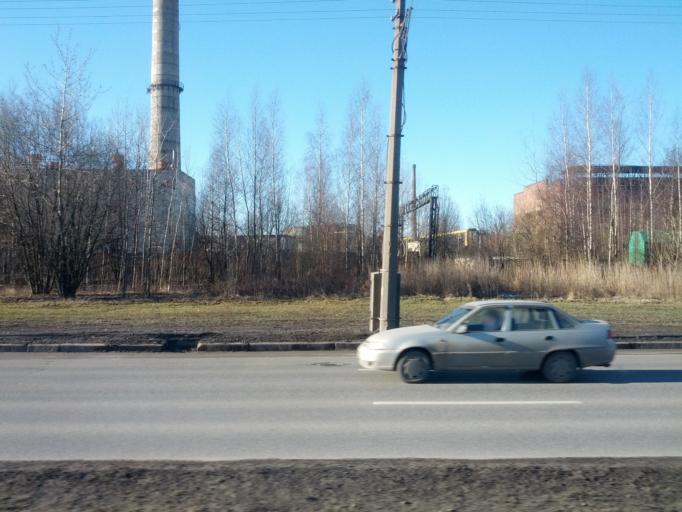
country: RU
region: St.-Petersburg
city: Obukhovo
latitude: 59.9065
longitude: 30.4514
